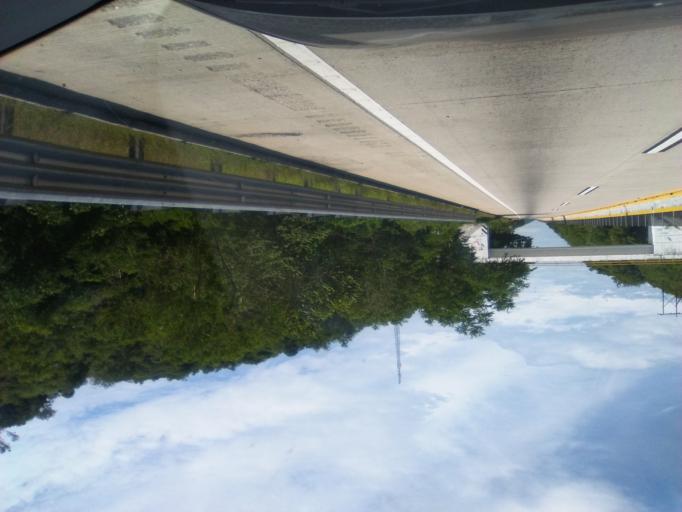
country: MX
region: Guerrero
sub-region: Acapulco de Juarez
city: Kilometro 30
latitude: 16.9992
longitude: -99.6910
